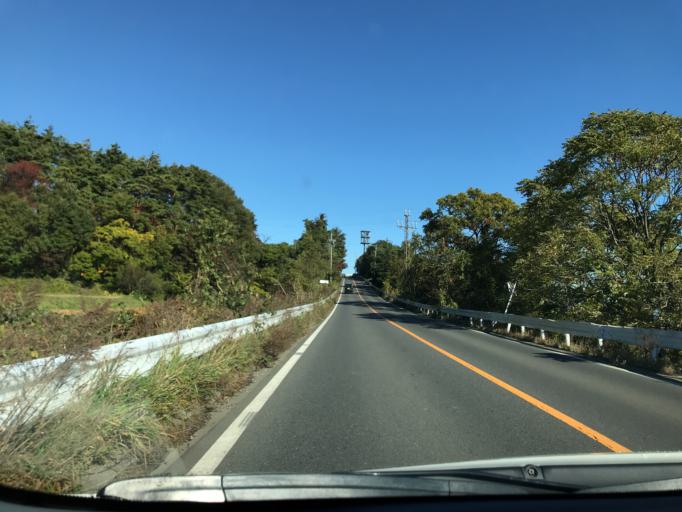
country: JP
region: Nagano
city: Shiojiri
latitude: 36.1289
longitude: 137.9246
